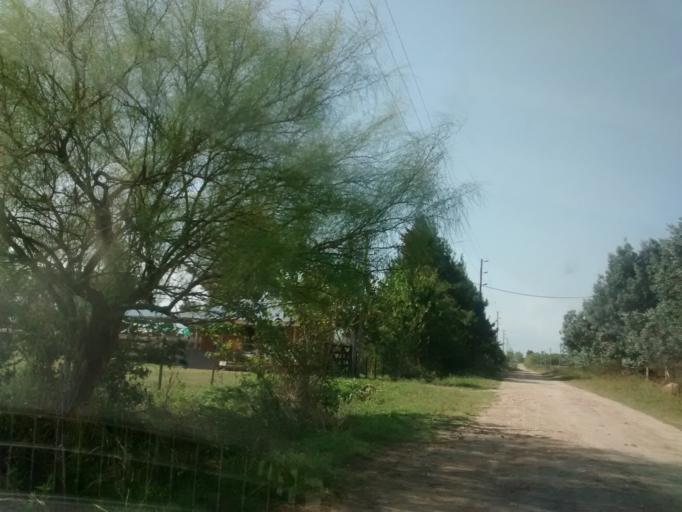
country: AR
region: Buenos Aires
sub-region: Partido de La Plata
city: La Plata
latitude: -35.0079
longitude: -57.9047
